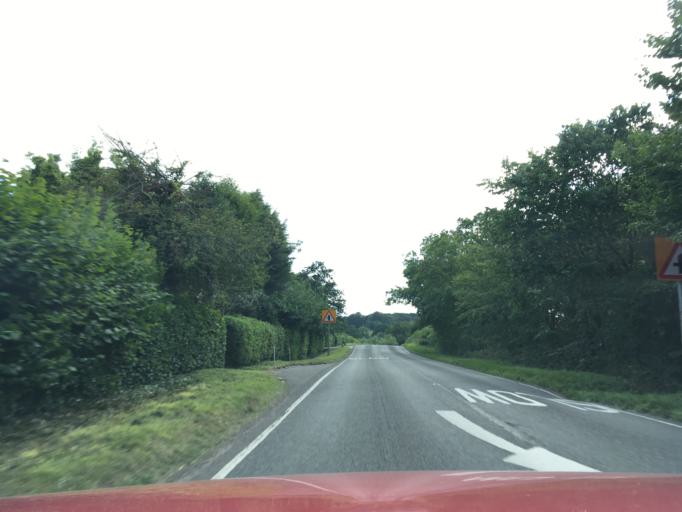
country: GB
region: England
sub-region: Leicestershire
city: Coalville
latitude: 52.7593
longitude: -1.4071
